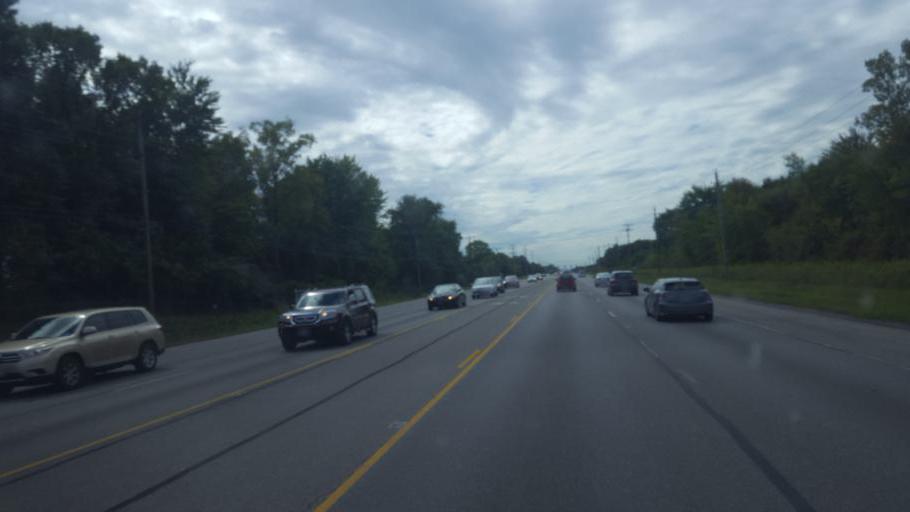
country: US
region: Ohio
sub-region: Franklin County
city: Reynoldsburg
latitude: 39.9876
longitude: -82.7705
